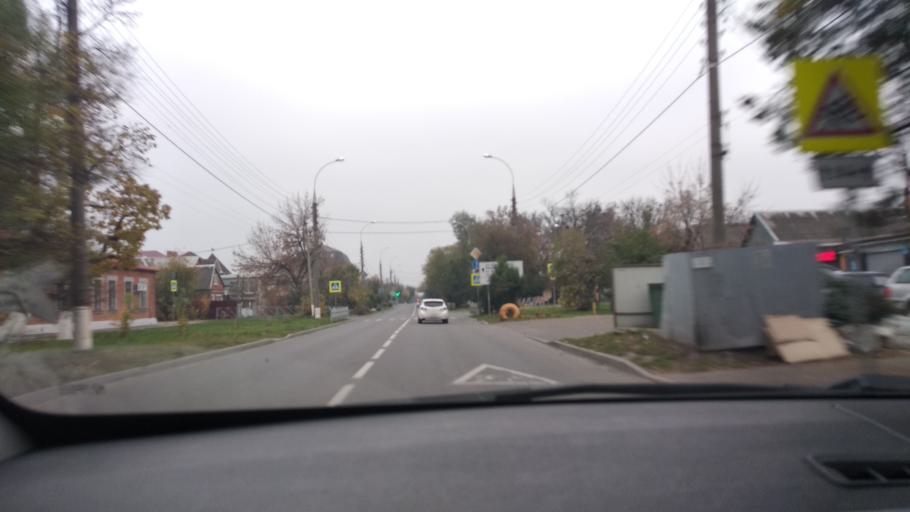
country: RU
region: Krasnodarskiy
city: Krasnodar
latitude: 45.0166
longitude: 39.0106
